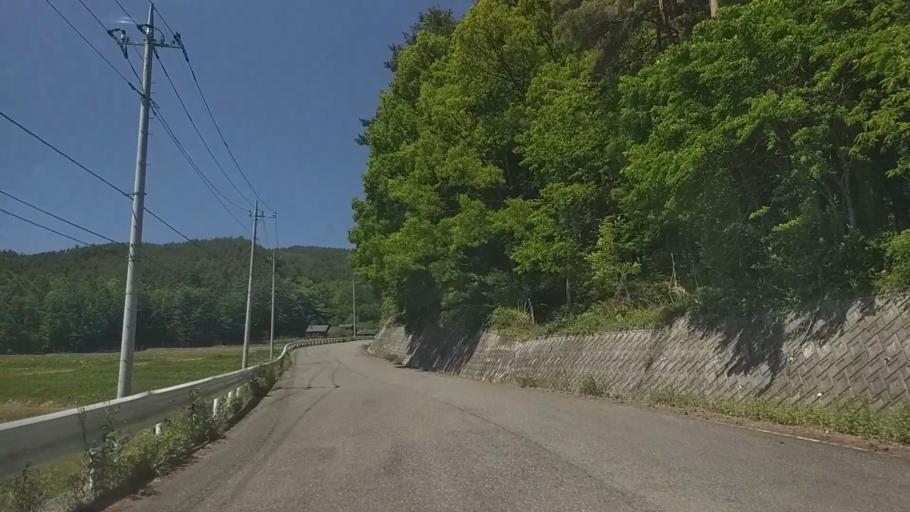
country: JP
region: Yamanashi
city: Nirasaki
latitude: 35.8582
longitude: 138.4473
